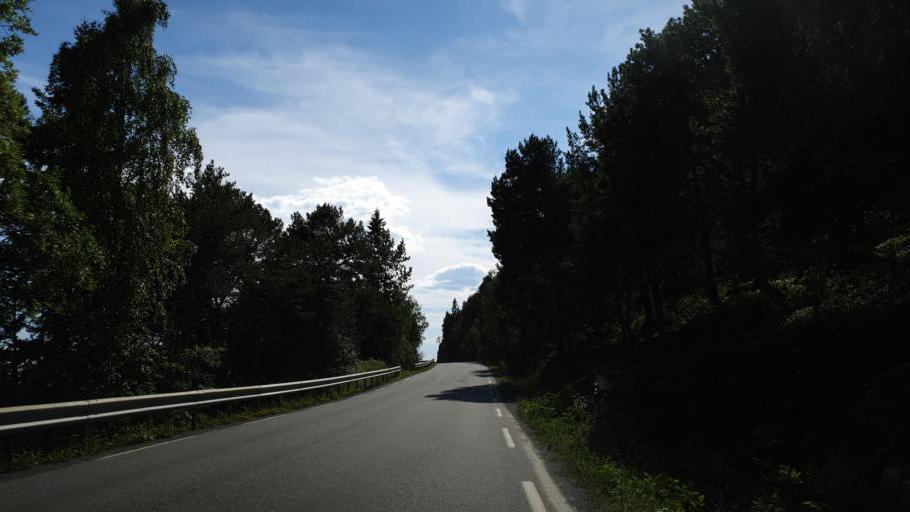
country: NO
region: Nord-Trondelag
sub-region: Leksvik
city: Leksvik
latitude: 63.6309
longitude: 10.5692
